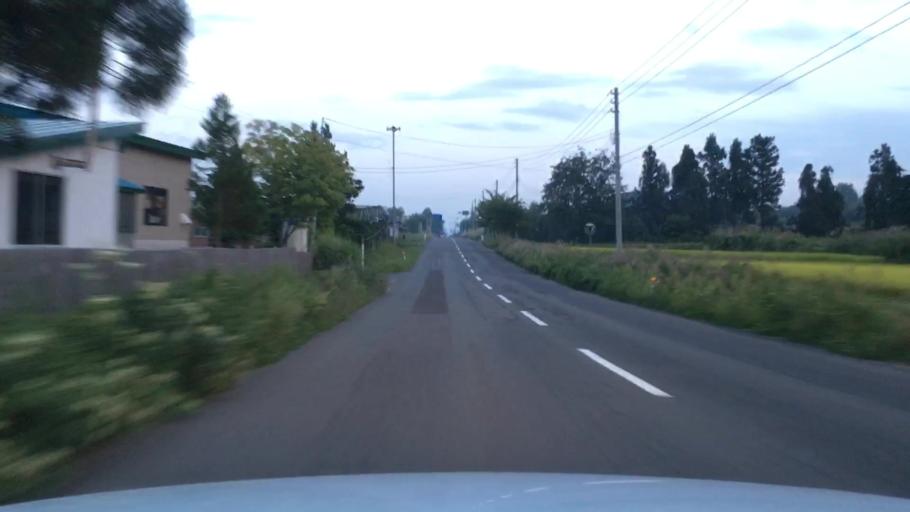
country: JP
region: Aomori
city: Hirosaki
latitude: 40.6804
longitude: 140.3717
